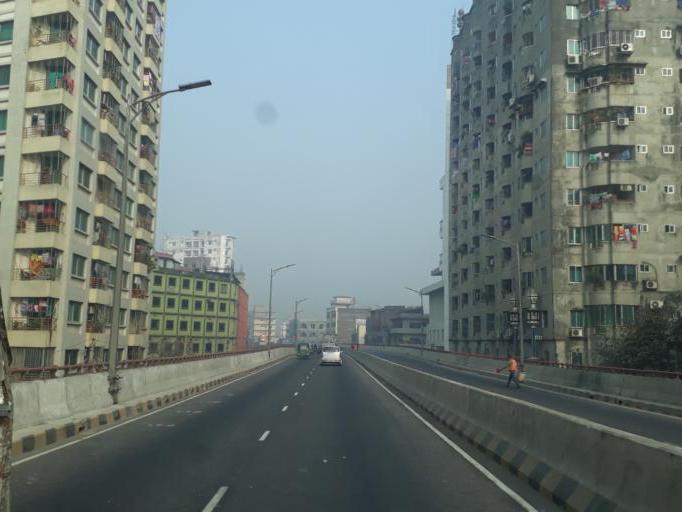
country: BD
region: Dhaka
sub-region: Dhaka
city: Dhaka
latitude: 23.7186
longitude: 90.4193
